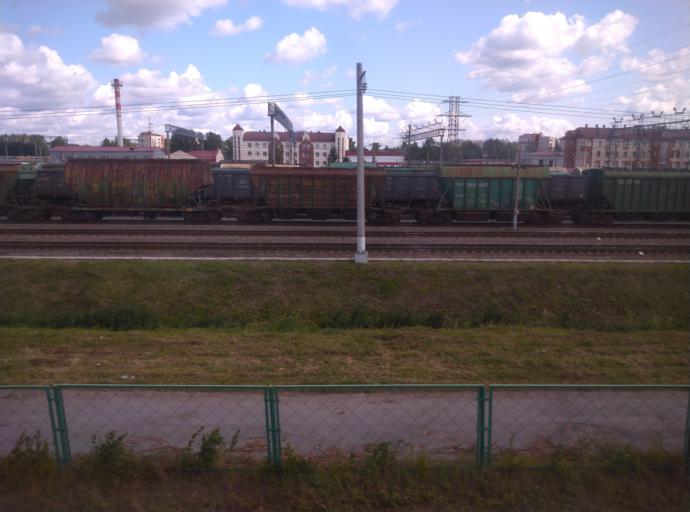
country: RU
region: St.-Petersburg
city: Obukhovo
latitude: 59.8633
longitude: 30.4310
